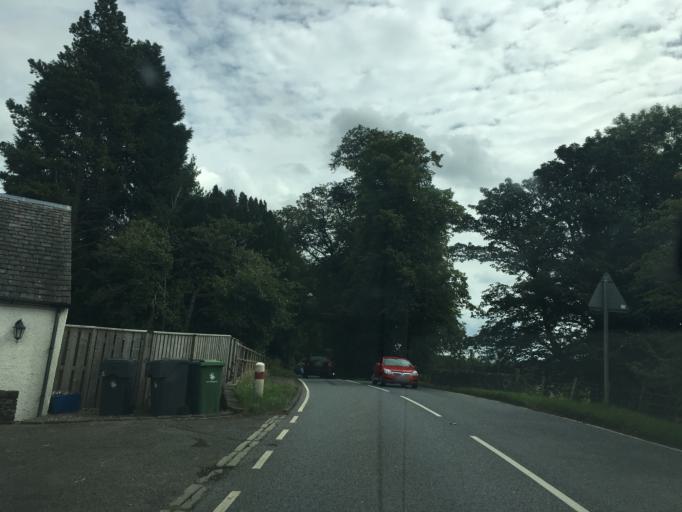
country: GB
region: Scotland
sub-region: Stirling
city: Callander
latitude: 56.2460
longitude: -4.2372
